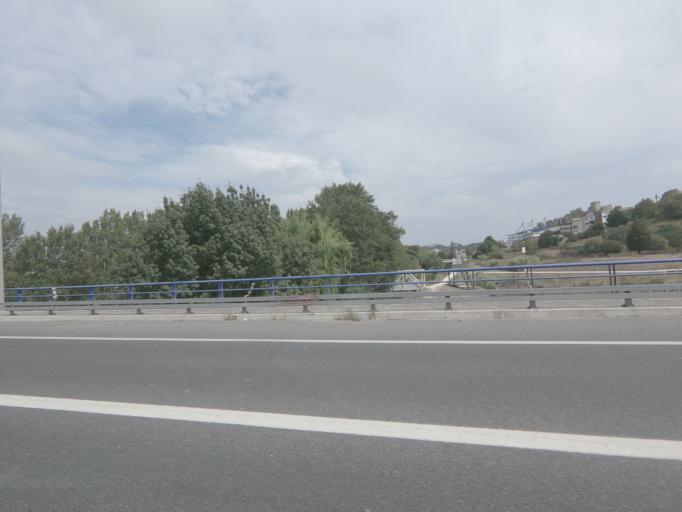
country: PT
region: Leiria
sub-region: Leiria
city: Leiria
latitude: 39.7517
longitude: -8.8172
